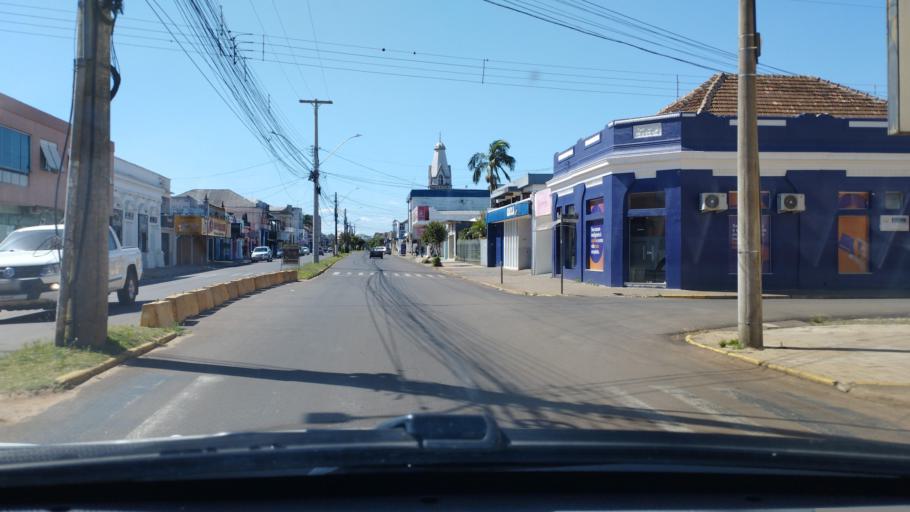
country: BR
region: Rio Grande do Sul
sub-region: Tupancireta
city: Tupancireta
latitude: -29.0826
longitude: -53.8361
